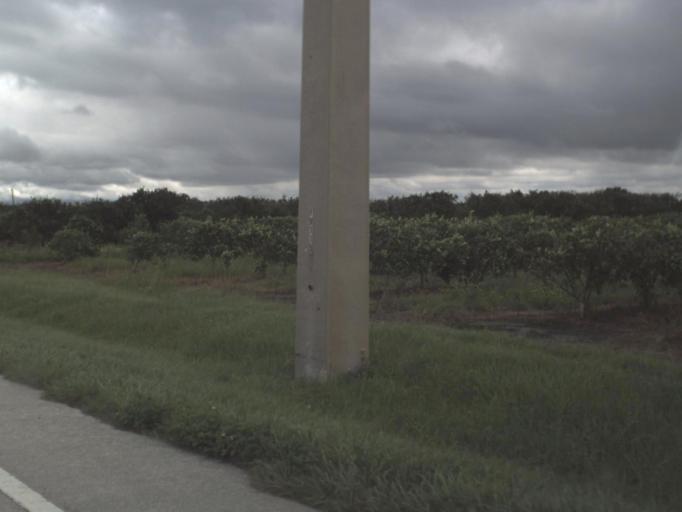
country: US
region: Florida
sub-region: Hardee County
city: Bowling Green
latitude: 27.5948
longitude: -81.8447
